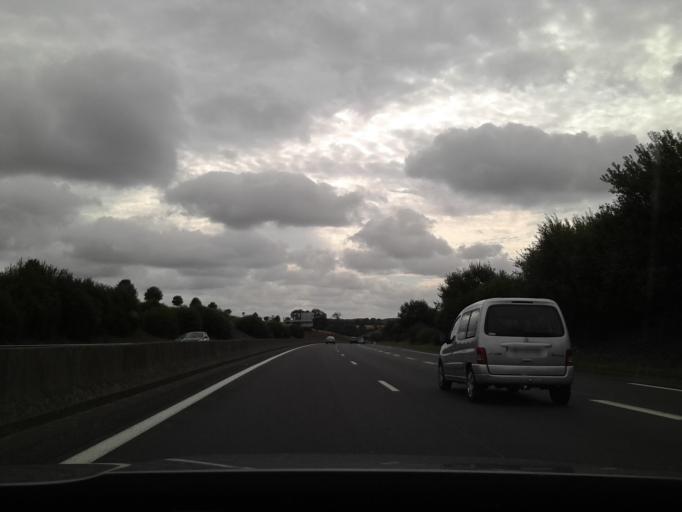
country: FR
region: Lower Normandy
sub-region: Departement du Calvados
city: Saint-Vigor-le-Grand
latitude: 49.2527
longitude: -0.6464
